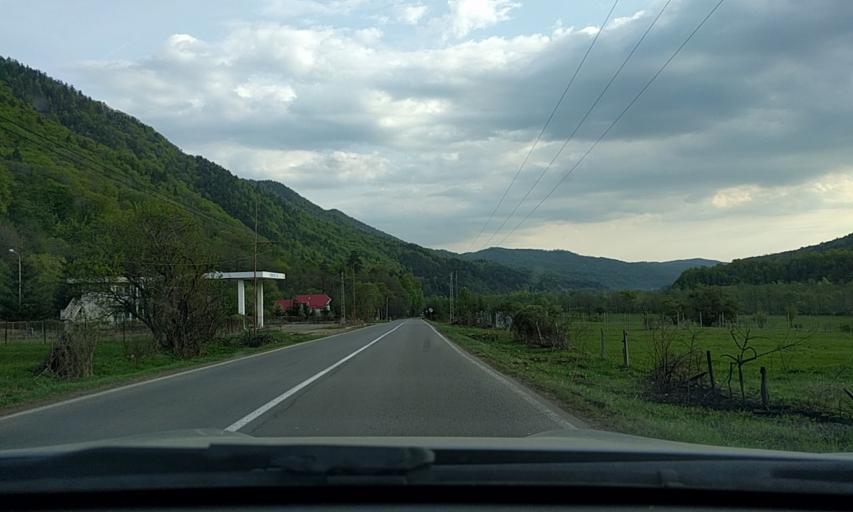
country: RO
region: Bacau
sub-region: Oras Slanic-Moldova
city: Slanic-Moldova
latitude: 46.1521
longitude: 26.4591
